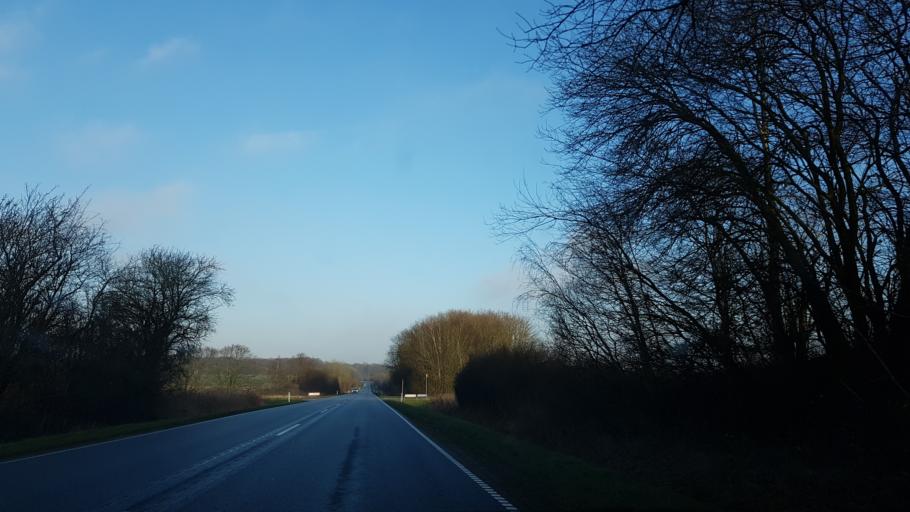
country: DK
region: South Denmark
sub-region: Haderslev Kommune
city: Vojens
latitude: 55.1812
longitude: 9.4003
